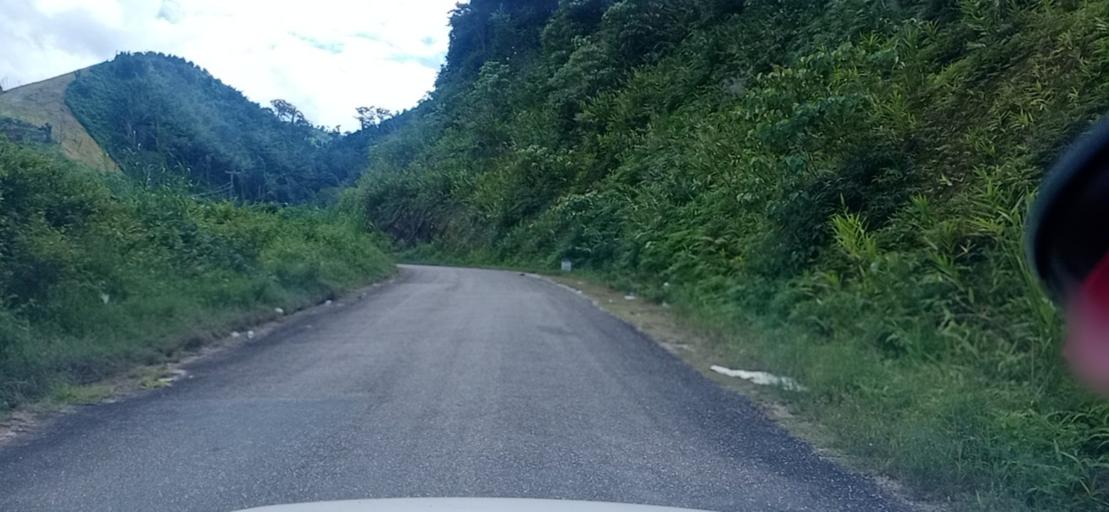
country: TH
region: Changwat Bueng Kan
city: Pak Khat
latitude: 18.6715
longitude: 103.1109
